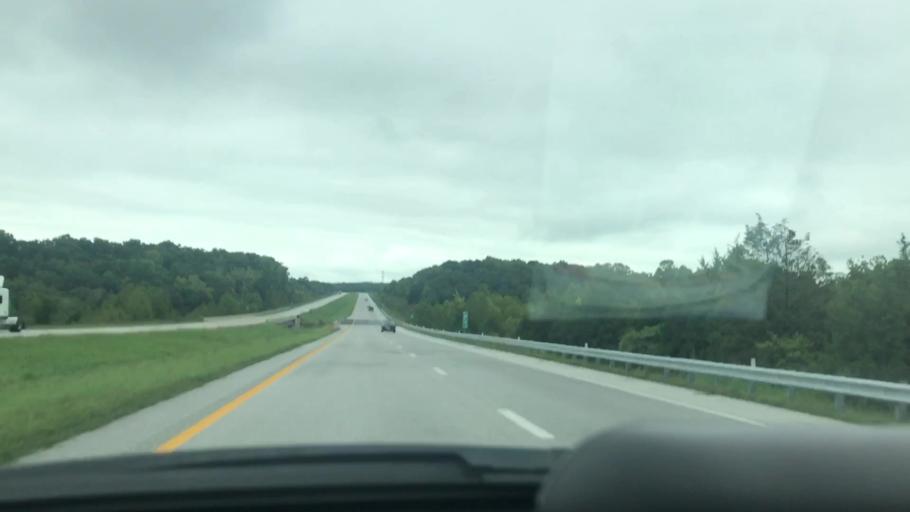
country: US
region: Missouri
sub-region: Greene County
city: Strafford
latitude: 37.3084
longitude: -93.1735
